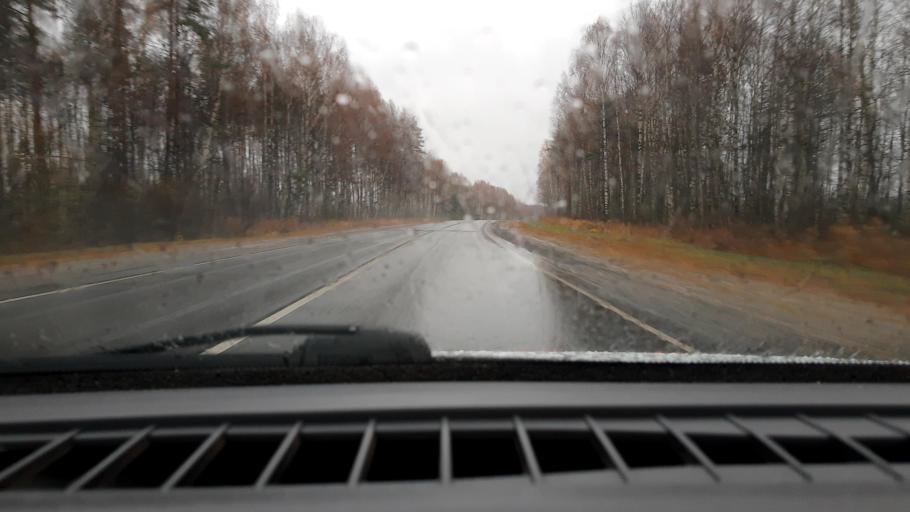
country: RU
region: Nizjnij Novgorod
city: Linda
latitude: 56.6487
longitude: 44.1151
